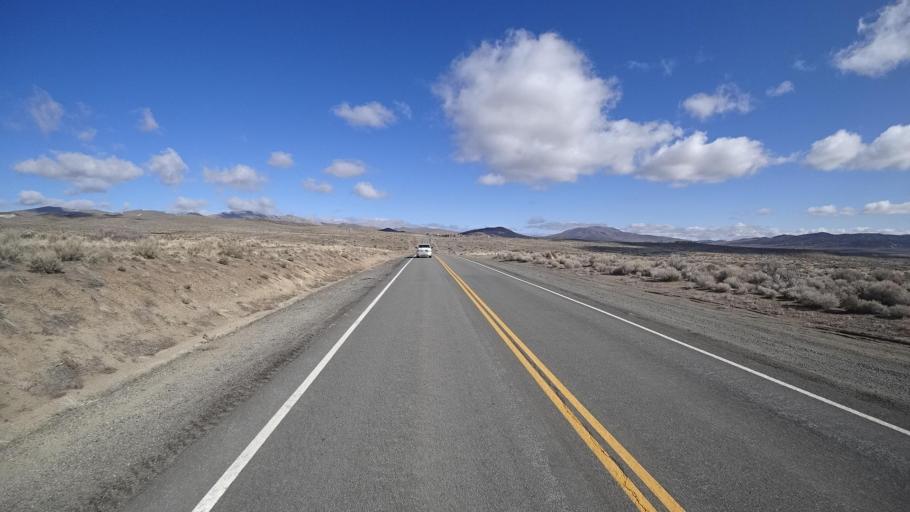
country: US
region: Nevada
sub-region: Washoe County
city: Cold Springs
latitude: 39.6735
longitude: -119.9225
